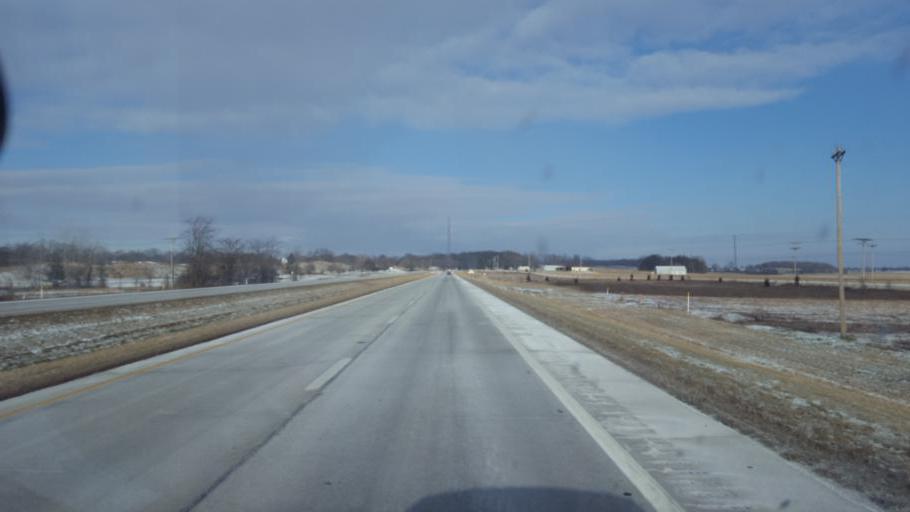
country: US
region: Ohio
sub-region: Pickaway County
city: South Bloomfield
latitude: 39.6865
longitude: -82.9797
